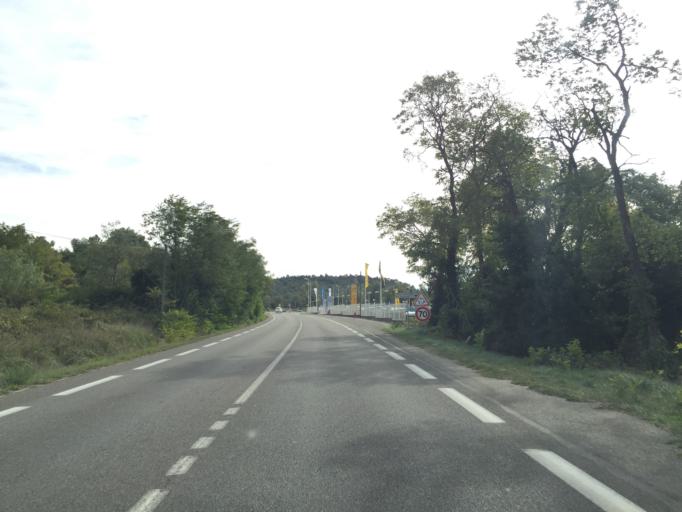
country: FR
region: Provence-Alpes-Cote d'Azur
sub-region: Departement du Vaucluse
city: Bollene
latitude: 44.2648
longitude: 4.7411
